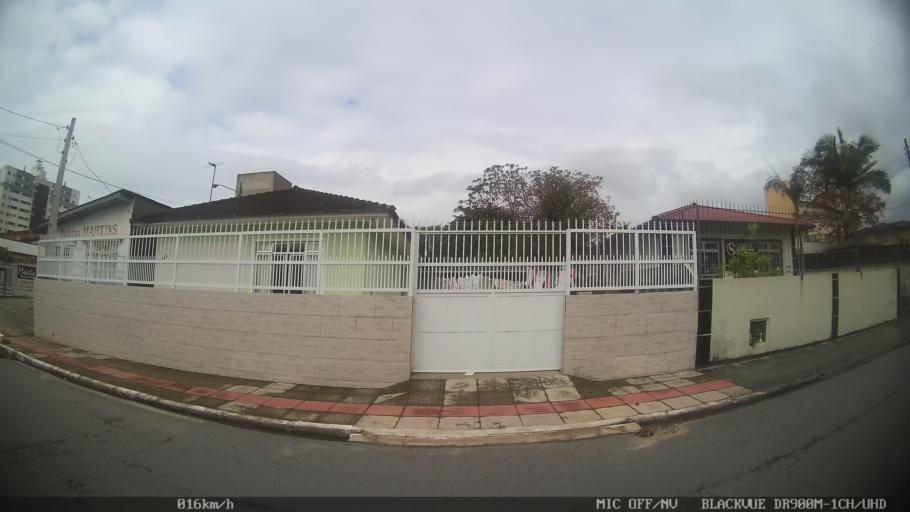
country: BR
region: Santa Catarina
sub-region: Sao Jose
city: Campinas
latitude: -27.5607
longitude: -48.6314
